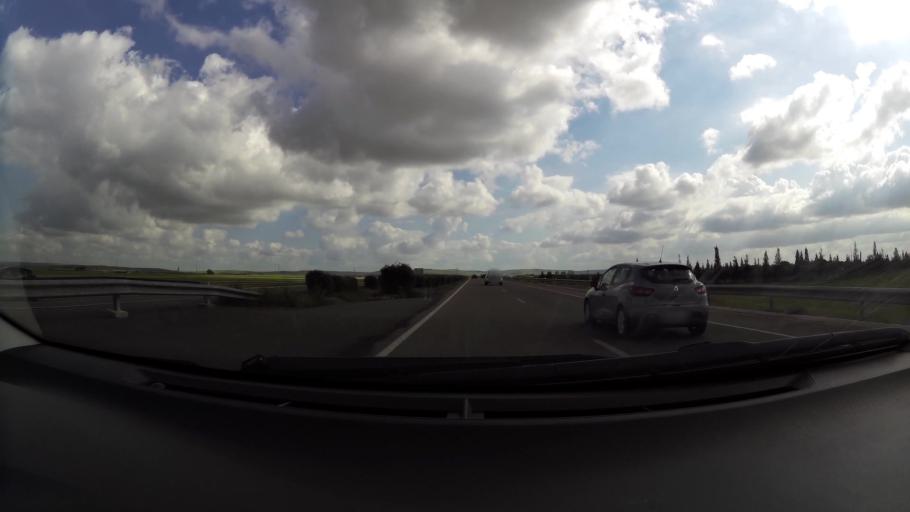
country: MA
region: Chaouia-Ouardigha
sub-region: Settat Province
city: Berrechid
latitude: 33.1309
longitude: -7.5786
